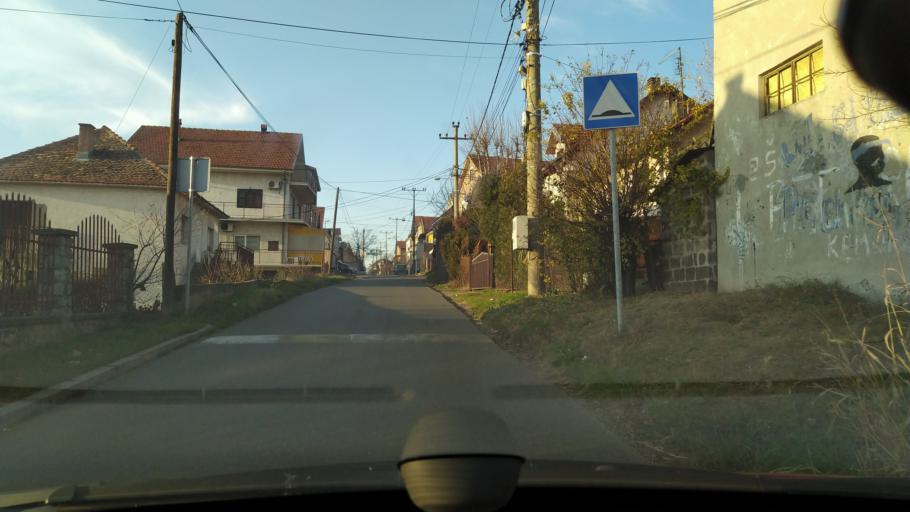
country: RS
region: Central Serbia
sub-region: Belgrade
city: Zvezdara
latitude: 44.7581
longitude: 20.5666
